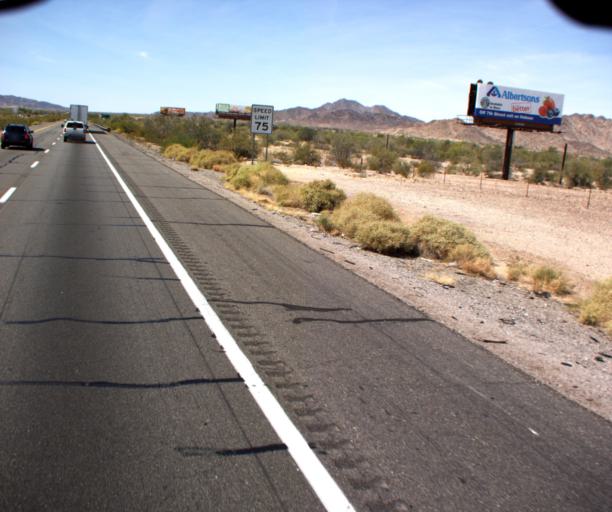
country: US
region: Arizona
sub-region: La Paz County
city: Quartzsite
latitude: 33.6583
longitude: -114.2520
